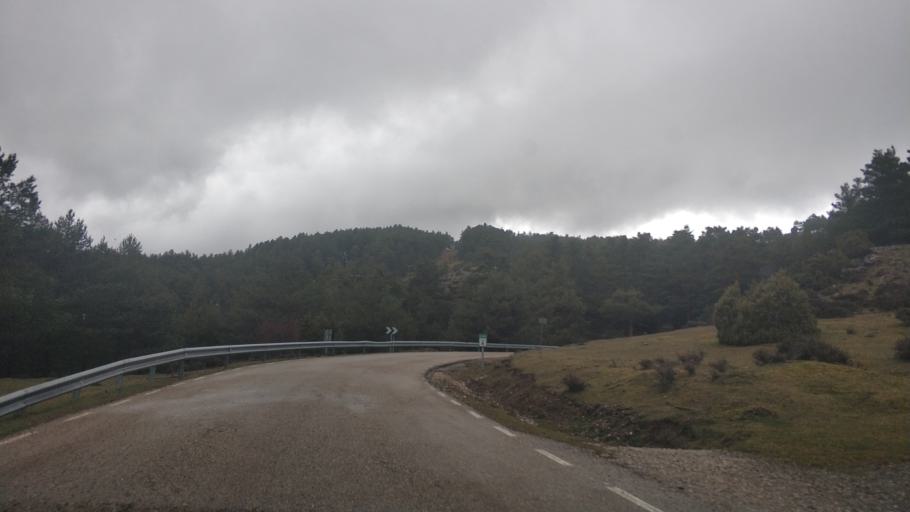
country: ES
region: Castille and Leon
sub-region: Provincia de Burgos
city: Neila
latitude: 42.0372
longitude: -3.0048
